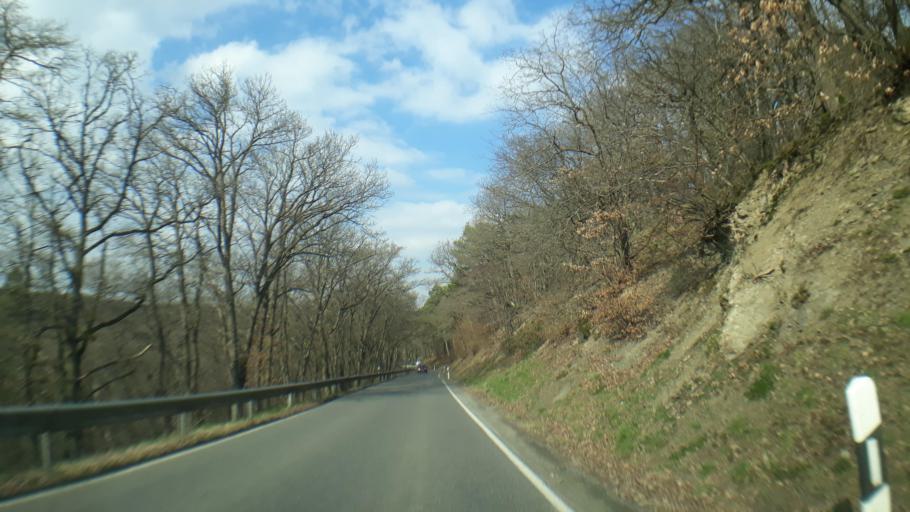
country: DE
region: Rheinland-Pfalz
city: Berg
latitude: 50.5550
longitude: 6.9434
